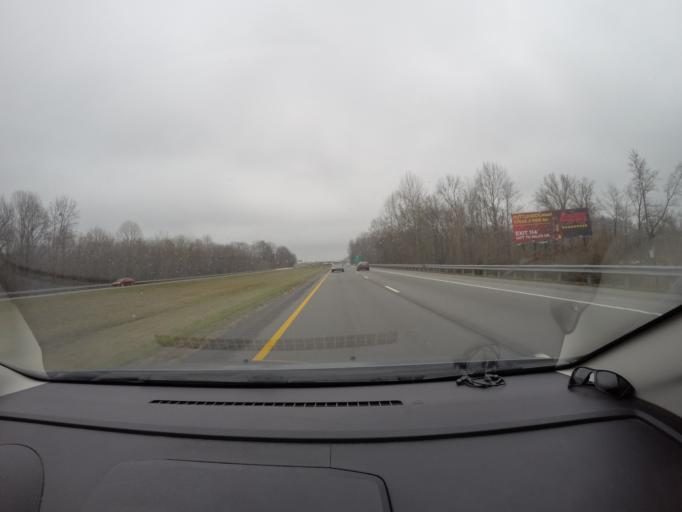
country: US
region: Tennessee
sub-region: Coffee County
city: Manchester
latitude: 35.5027
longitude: -86.0930
